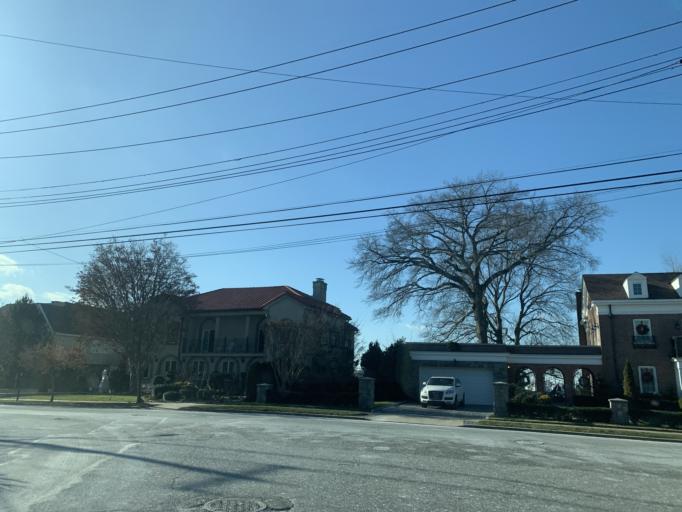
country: US
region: New York
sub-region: Bronx
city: The Bronx
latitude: 40.7936
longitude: -73.8268
